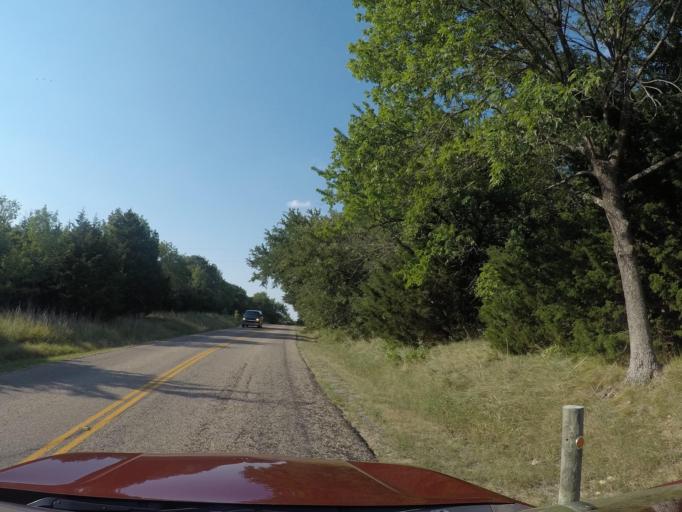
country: US
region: Texas
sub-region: Grayson County
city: Preston
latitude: 33.8154
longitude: -96.6097
